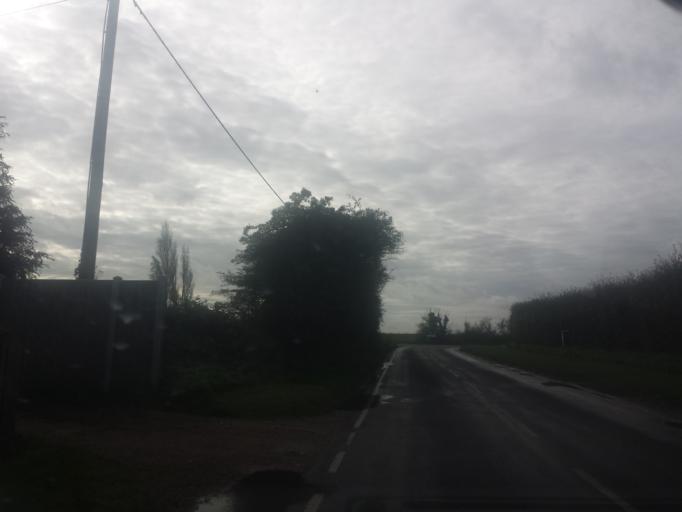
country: GB
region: England
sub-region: Essex
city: Saint Osyth
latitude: 51.7936
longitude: 1.0636
